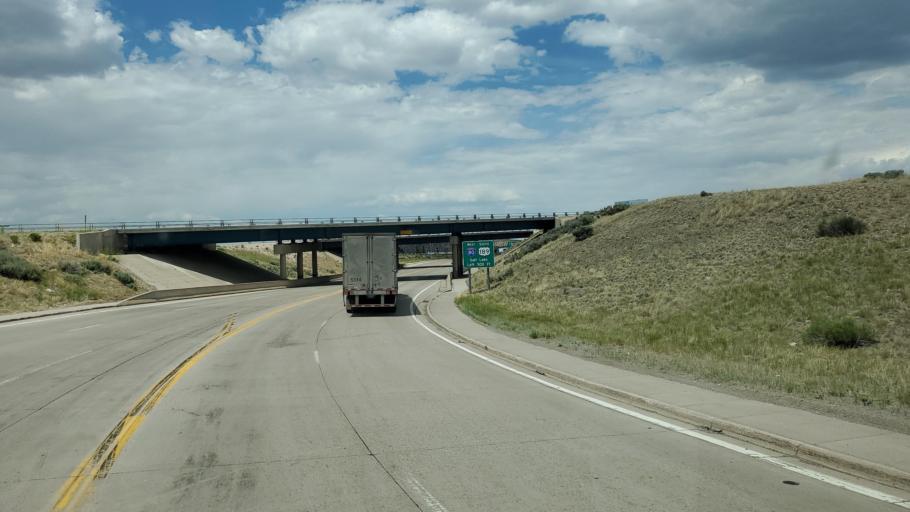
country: US
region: Wyoming
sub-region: Uinta County
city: Evanston
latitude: 41.2598
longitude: -110.9859
